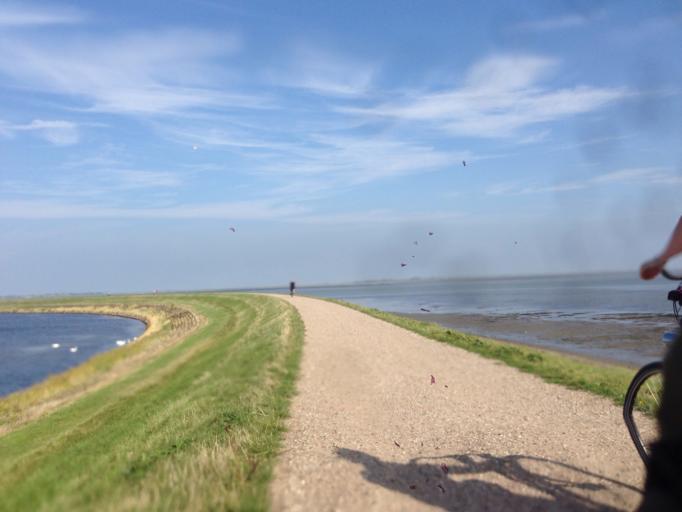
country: DE
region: Schleswig-Holstein
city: Tinnum
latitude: 54.8622
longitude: 8.3288
